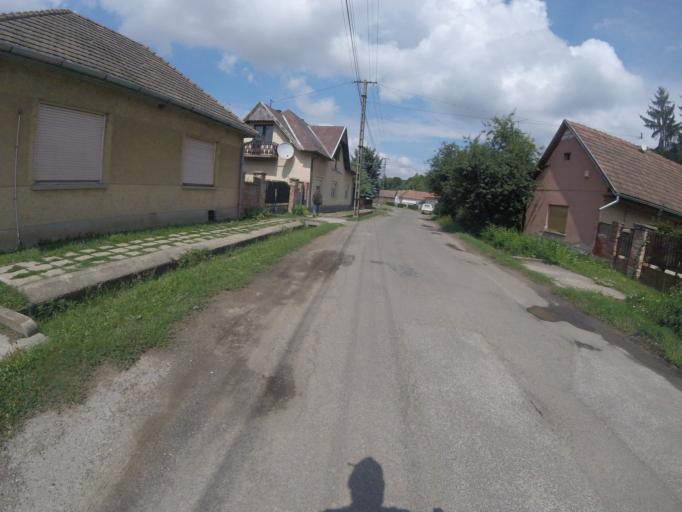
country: SK
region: Nitriansky
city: Sahy
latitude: 48.0368
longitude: 18.9161
